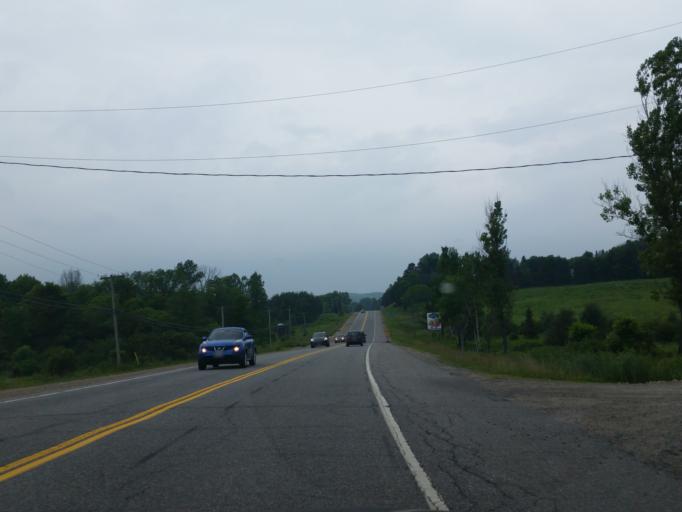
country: CA
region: Ontario
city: Huntsville
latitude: 45.3540
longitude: -79.0896
